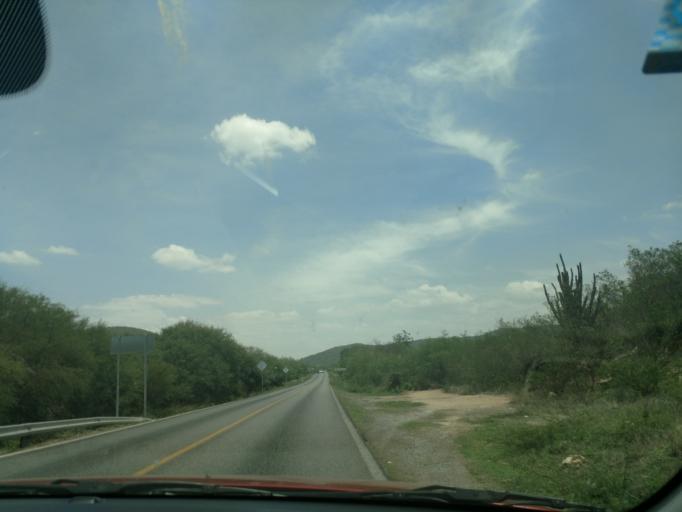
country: MX
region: San Luis Potosi
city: Ciudad Fernandez
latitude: 22.0044
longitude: -100.1461
